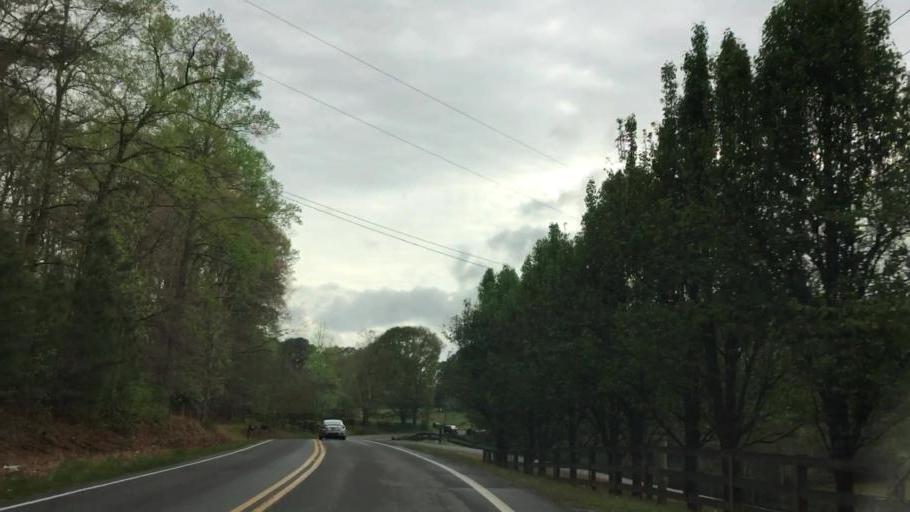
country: US
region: Georgia
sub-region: Fulton County
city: Milton
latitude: 34.1987
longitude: -84.3730
